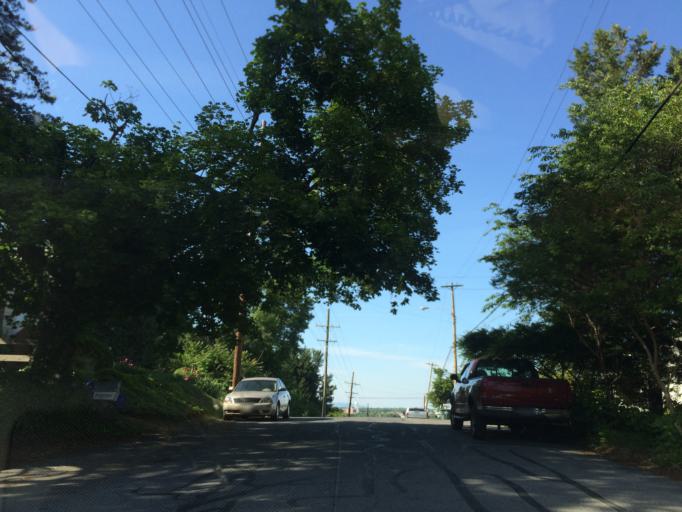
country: US
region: Maryland
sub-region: Frederick County
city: Frederick
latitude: 39.4130
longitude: -77.4397
